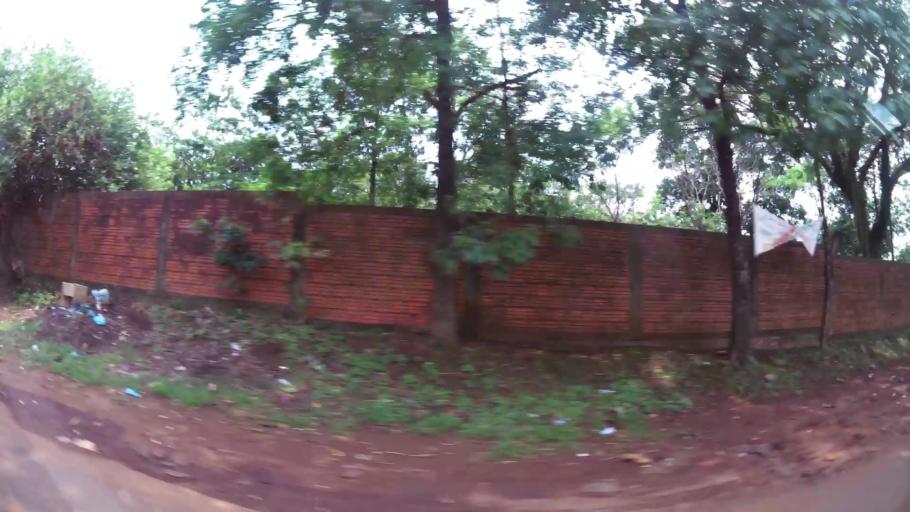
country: PY
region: Alto Parana
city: Presidente Franco
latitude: -25.5532
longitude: -54.6413
